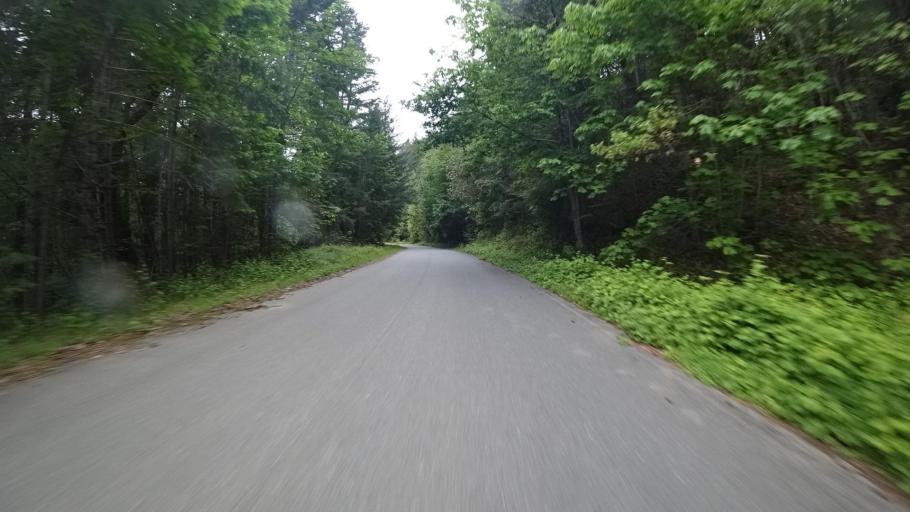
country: US
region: California
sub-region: Humboldt County
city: Willow Creek
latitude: 41.1195
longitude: -123.7371
